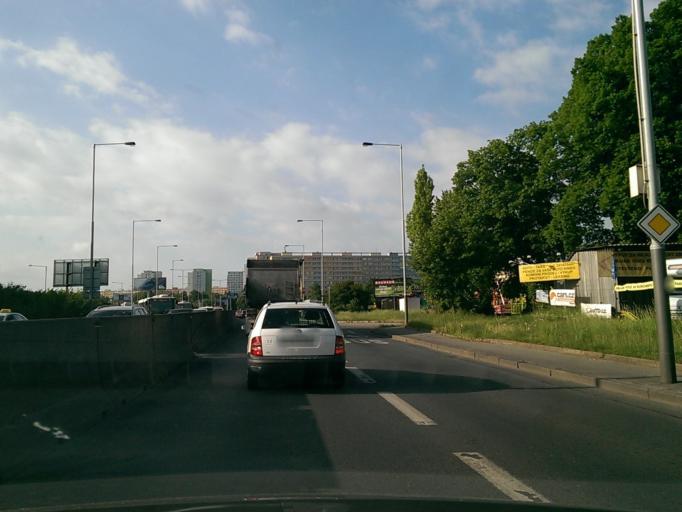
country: CZ
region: Praha
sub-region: Praha 4
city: Hodkovicky
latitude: 50.0319
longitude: 14.4550
